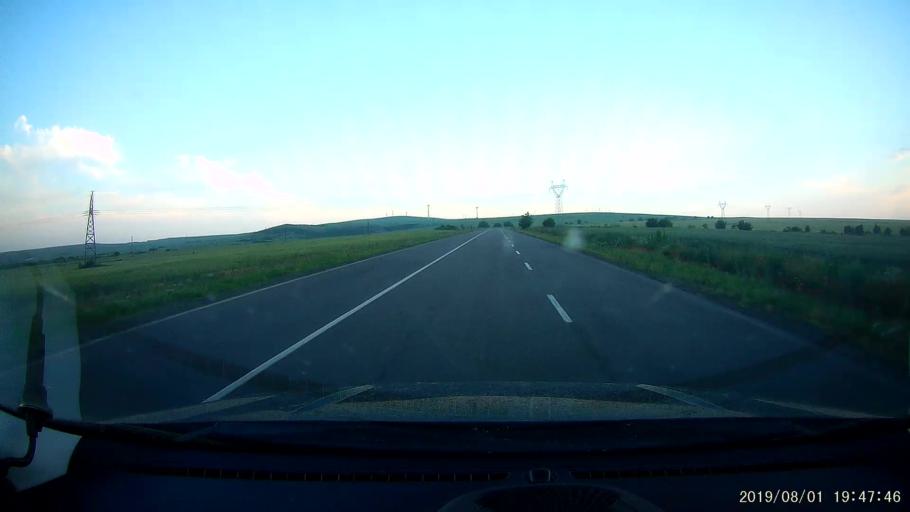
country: BG
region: Burgas
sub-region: Obshtina Karnobat
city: Karnobat
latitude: 42.6469
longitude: 26.9579
